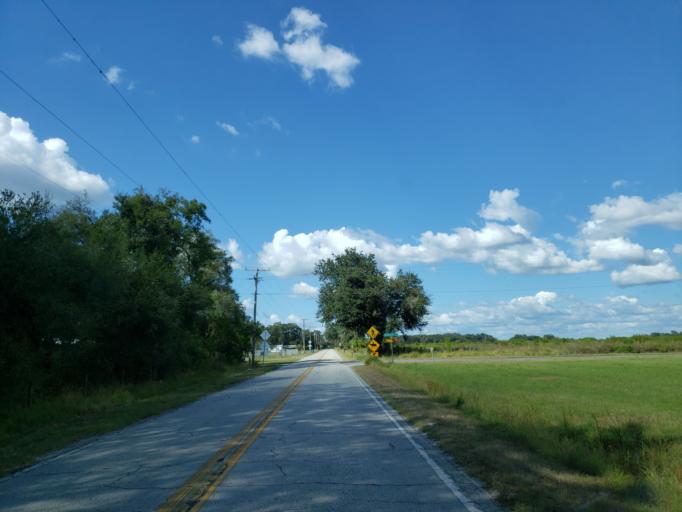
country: US
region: Florida
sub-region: Hillsborough County
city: Valrico
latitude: 27.9519
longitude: -82.2031
